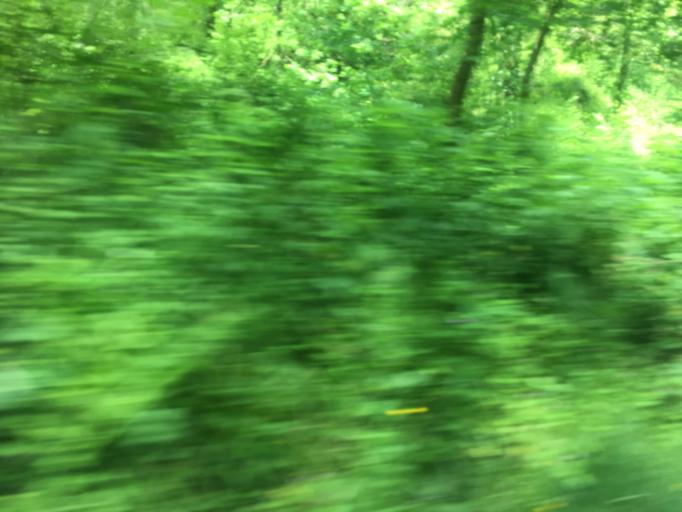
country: GB
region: Wales
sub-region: Carmarthenshire
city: Llansadwrn
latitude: 51.9935
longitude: -3.8906
